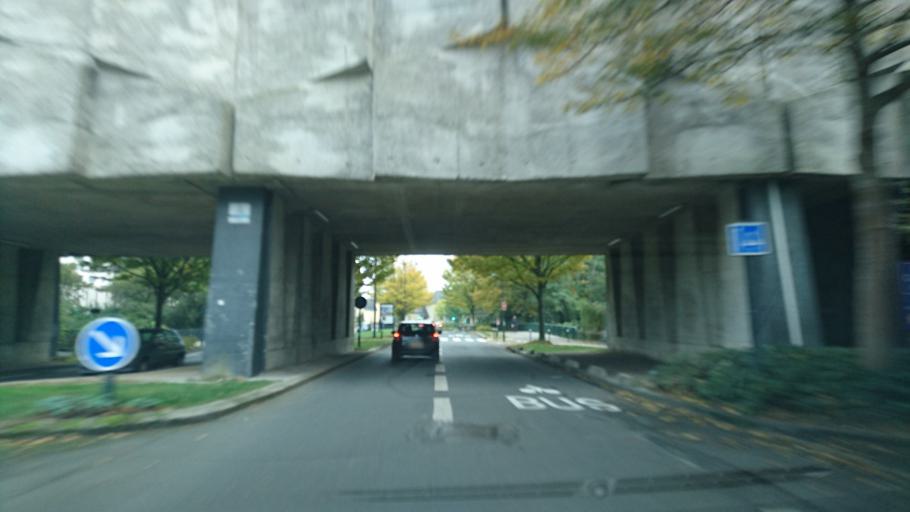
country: FR
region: Brittany
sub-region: Departement d'Ille-et-Vilaine
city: Rennes
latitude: 48.1125
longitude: -1.6921
